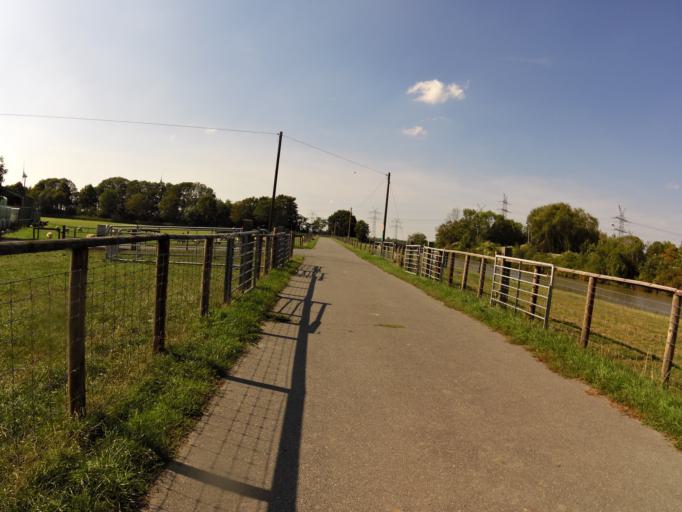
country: DE
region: Lower Saxony
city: Nordenham
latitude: 53.4249
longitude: 8.4712
